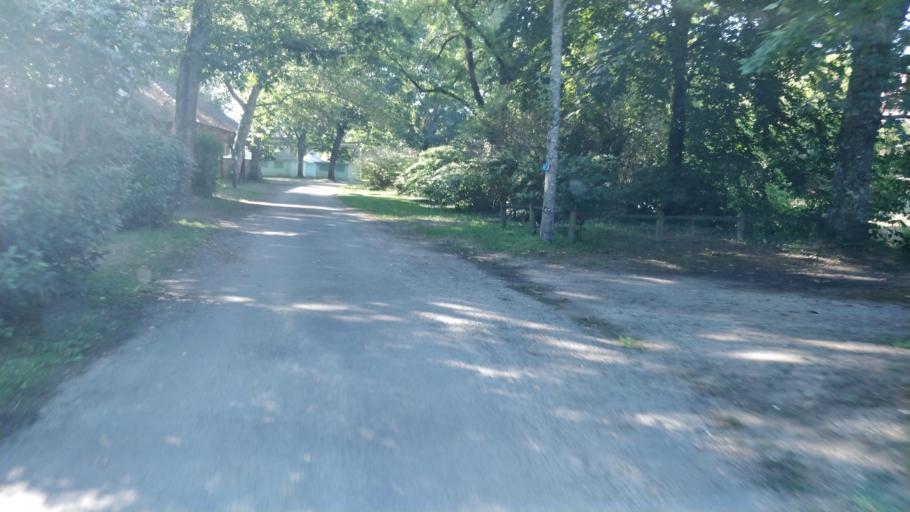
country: FR
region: Limousin
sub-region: Departement de la Correze
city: Beaulieu-sur-Dordogne
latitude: 44.9787
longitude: 1.8417
